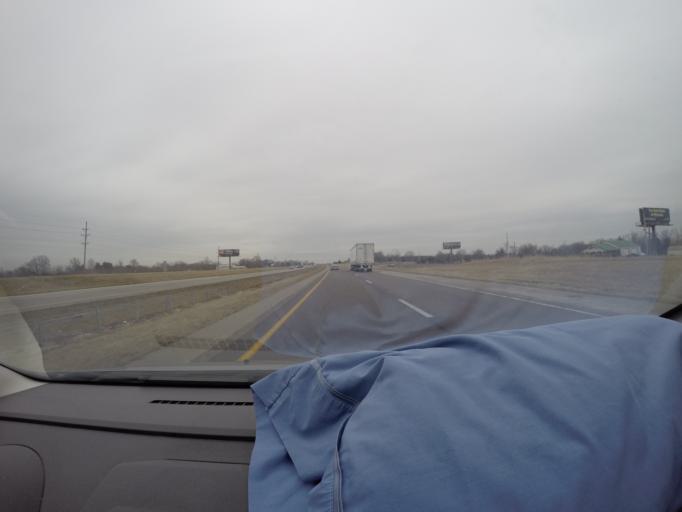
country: US
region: Missouri
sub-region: Saint Charles County
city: Wentzville
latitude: 38.8095
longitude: -90.9271
